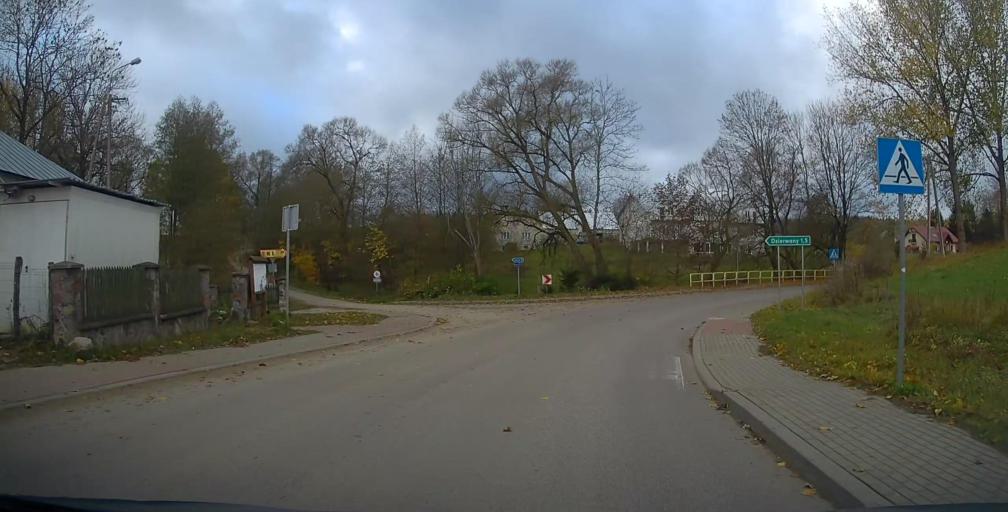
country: PL
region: Podlasie
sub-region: Suwalki
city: Suwalki
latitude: 54.2873
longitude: 22.8818
